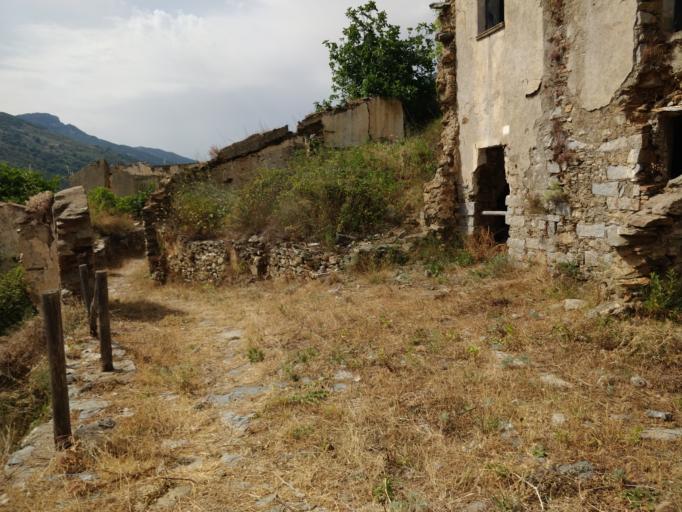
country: IT
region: Sardinia
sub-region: Provincia di Ogliastra
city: Gairo Sant'Elena
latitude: 39.8459
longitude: 9.5006
